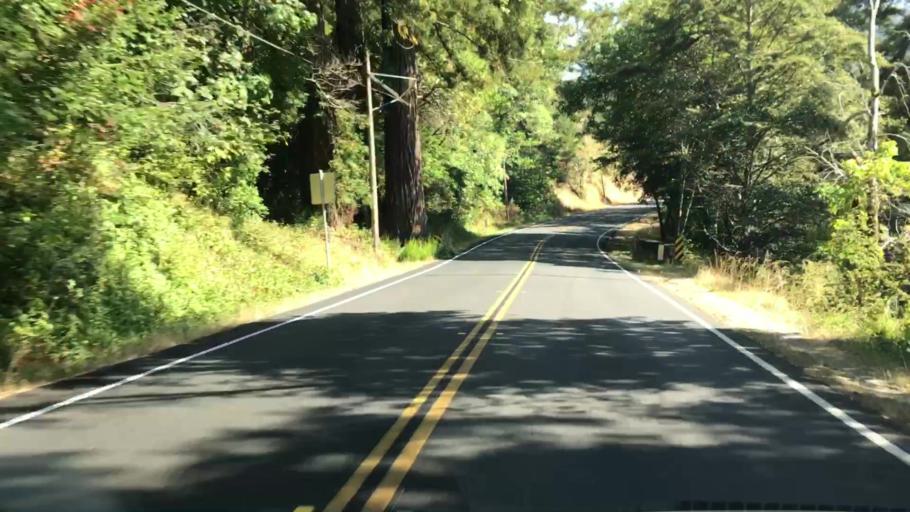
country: US
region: California
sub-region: Marin County
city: Lagunitas-Forest Knolls
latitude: 38.0283
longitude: -122.7358
